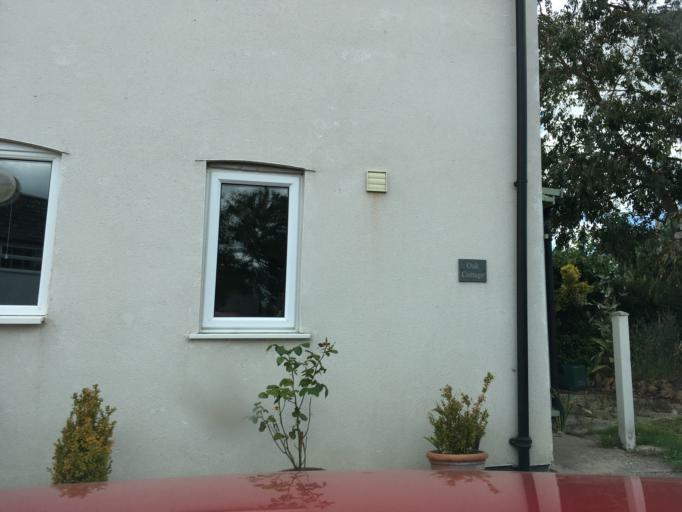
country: GB
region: England
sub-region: Oxfordshire
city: Faringdon
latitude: 51.6164
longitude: -1.6066
